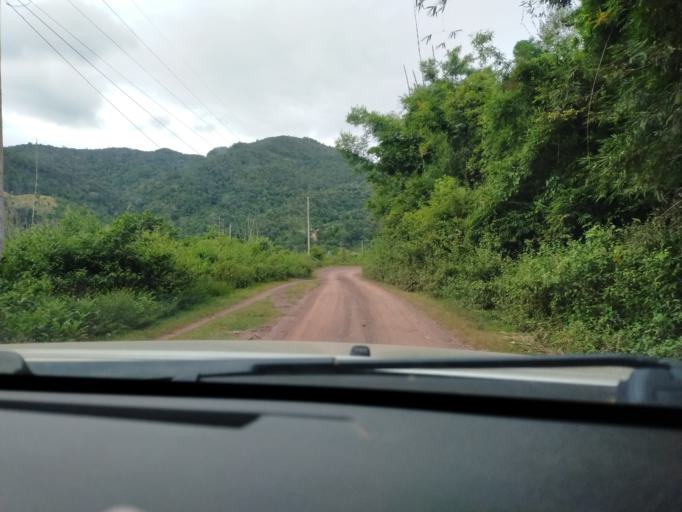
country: TH
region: Nan
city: Chaloem Phra Kiat
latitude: 19.7697
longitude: 101.3498
